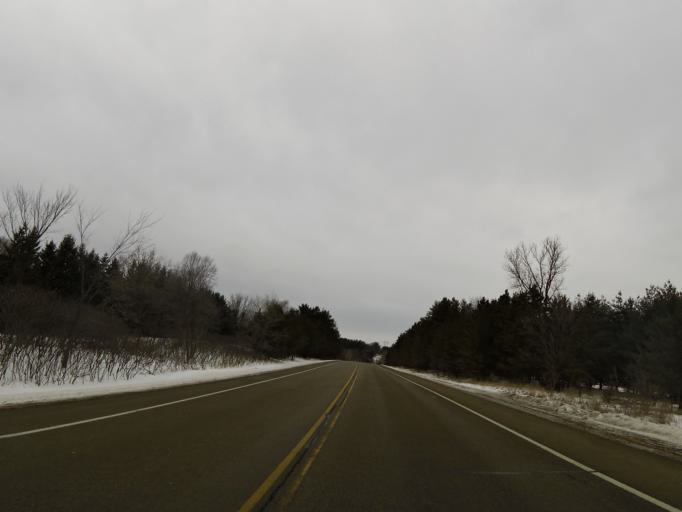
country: US
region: Minnesota
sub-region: Washington County
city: Bayport
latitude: 45.0291
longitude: -92.7486
